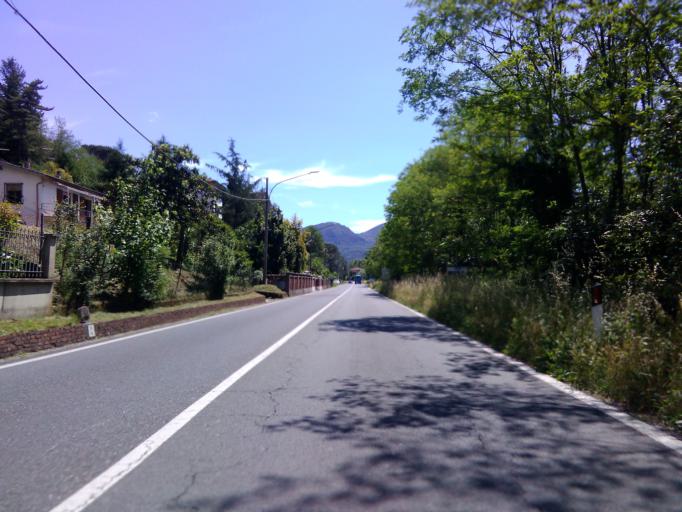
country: IT
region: Tuscany
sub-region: Provincia di Massa-Carrara
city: Terrarossa
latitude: 44.2355
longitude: 9.9602
